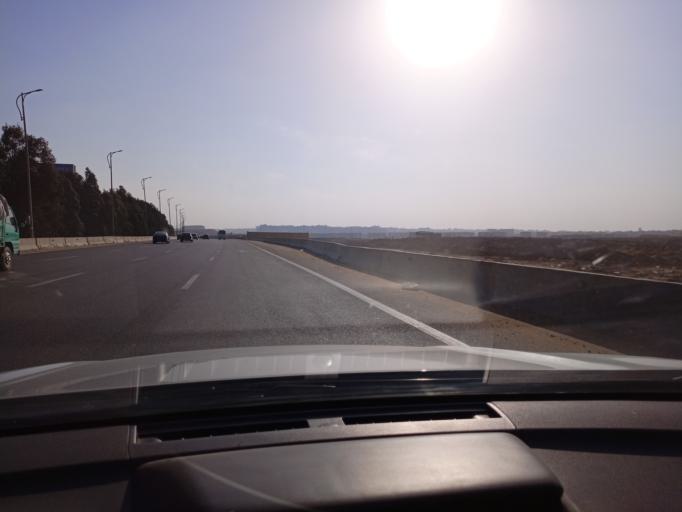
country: EG
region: Muhafazat al Qalyubiyah
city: Al Khankah
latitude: 30.0661
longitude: 31.4212
